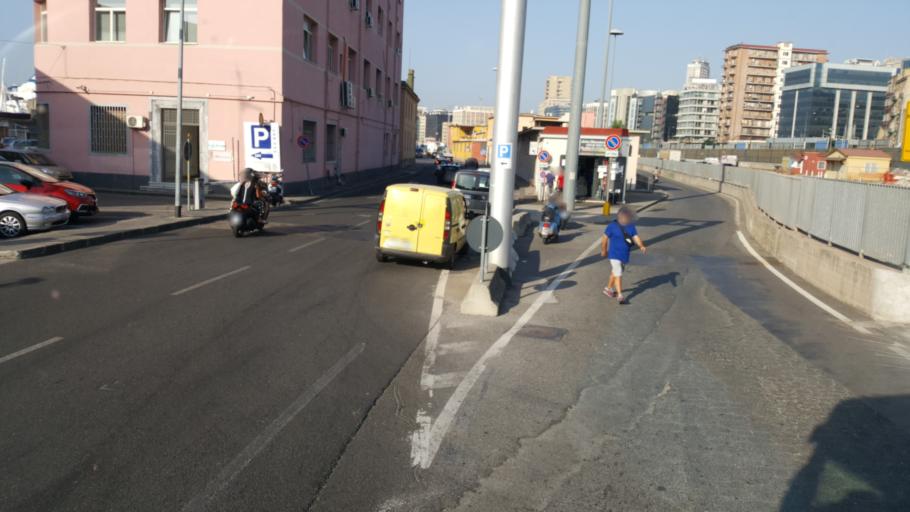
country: IT
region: Campania
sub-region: Provincia di Napoli
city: Napoli
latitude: 40.8451
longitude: 14.2625
